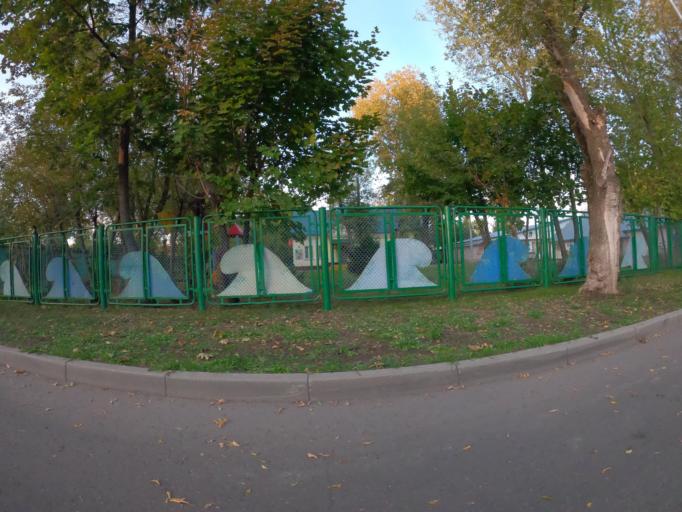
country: RU
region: Moskovskaya
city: Kur'yanovo
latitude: 55.6537
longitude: 37.6962
